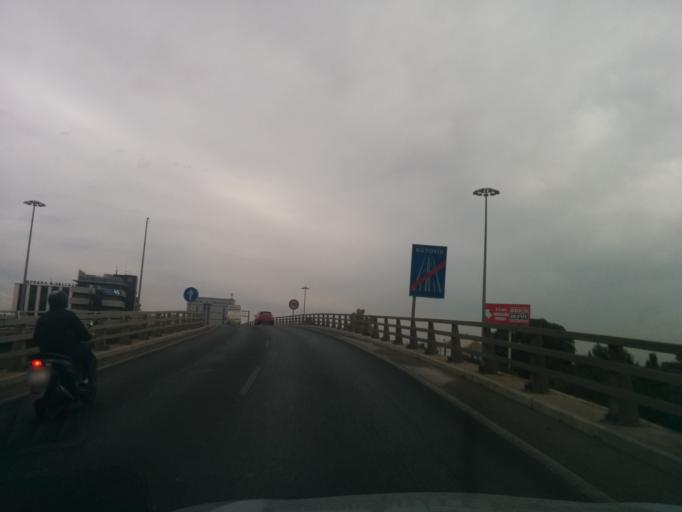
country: ES
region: Andalusia
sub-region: Provincia de Sevilla
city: Sevilla
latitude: 37.4071
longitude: -5.9486
